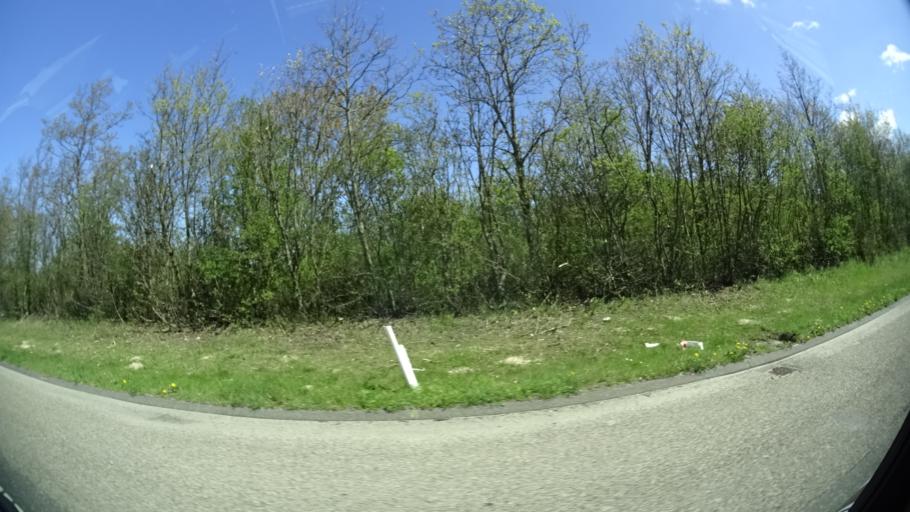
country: DK
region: Central Jutland
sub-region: Skanderborg Kommune
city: Horning
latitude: 56.1146
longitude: 10.0387
